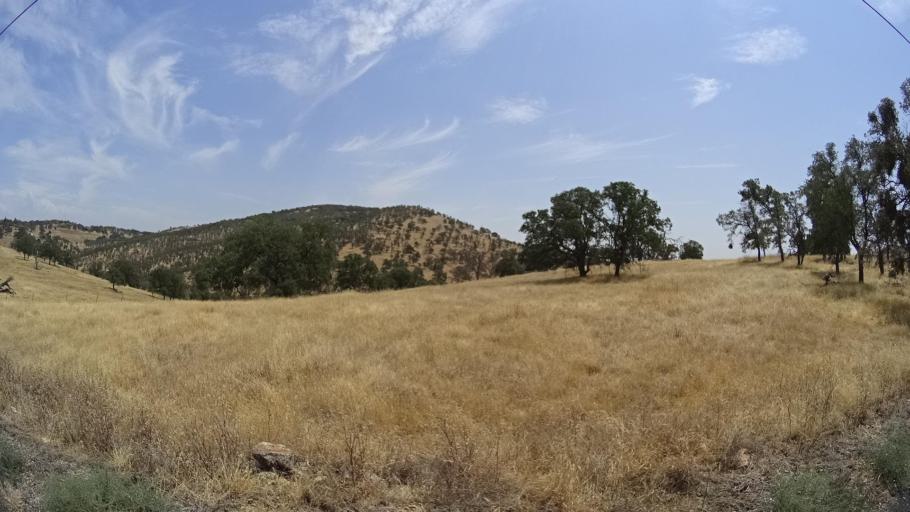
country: US
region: California
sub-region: Tuolumne County
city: Jamestown
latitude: 37.6373
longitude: -120.3256
